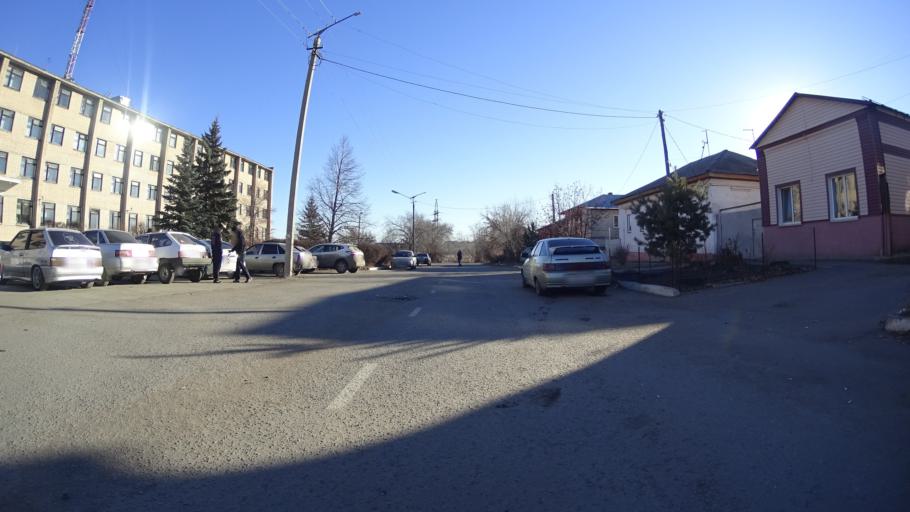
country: RU
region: Chelyabinsk
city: Troitsk
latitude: 54.0809
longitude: 61.5620
